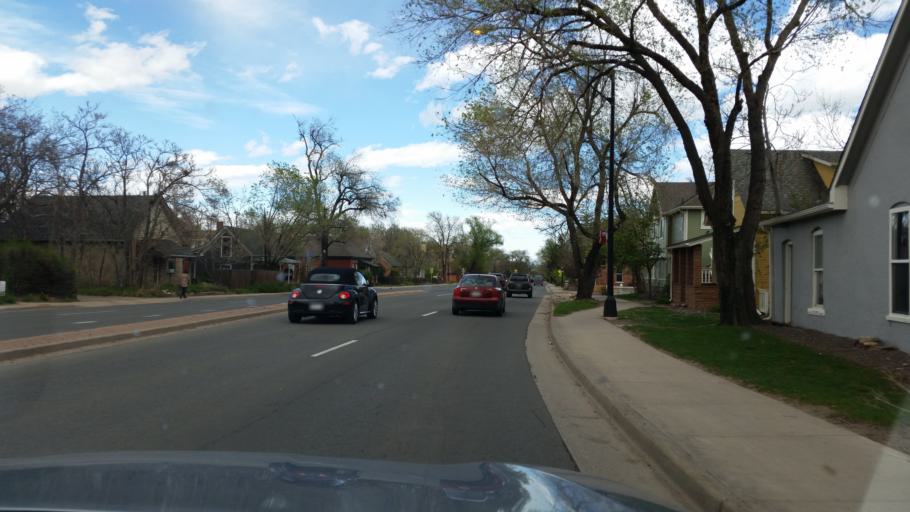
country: US
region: Colorado
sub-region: Boulder County
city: Boulder
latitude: 40.0172
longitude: -105.2727
